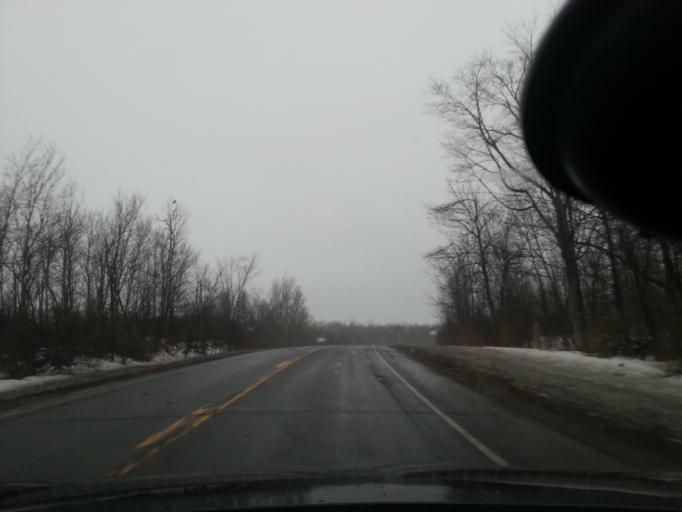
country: US
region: New York
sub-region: St. Lawrence County
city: Canton
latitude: 44.5071
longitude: -75.3399
